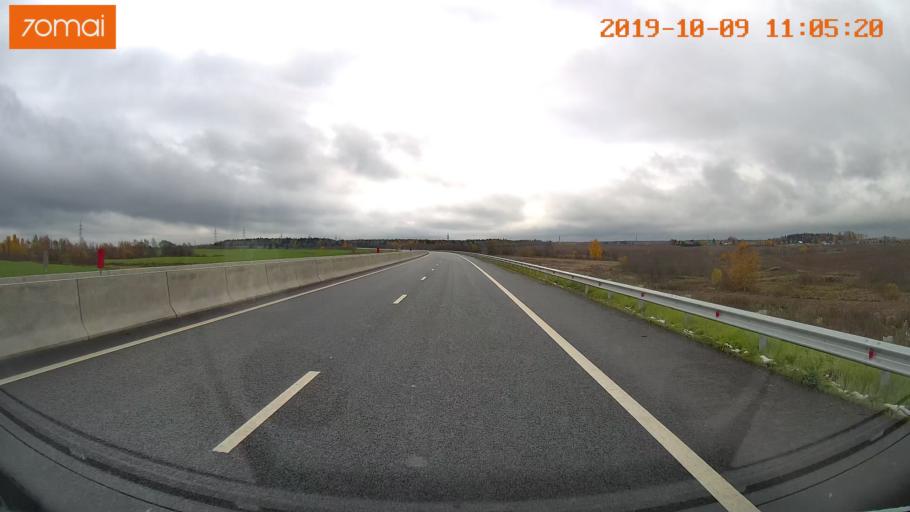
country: RU
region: Vologda
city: Molochnoye
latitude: 59.2017
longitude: 39.7592
